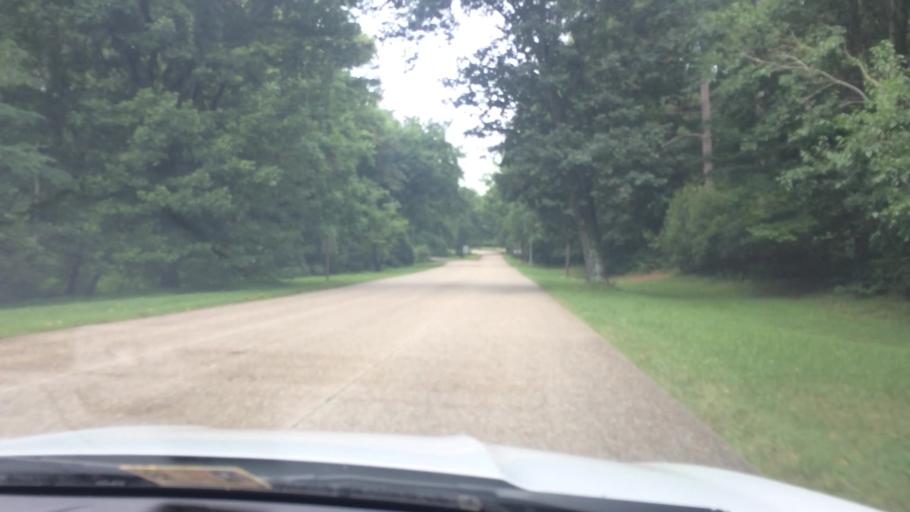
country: US
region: Virginia
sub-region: City of Williamsburg
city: Williamsburg
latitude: 37.2781
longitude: -76.6950
